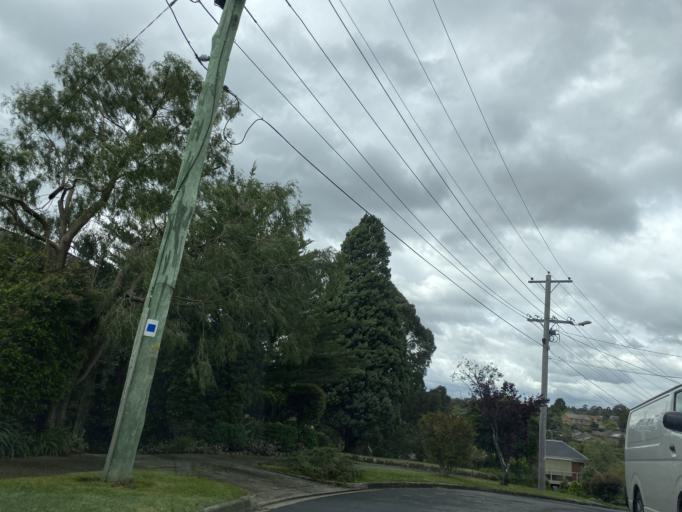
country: AU
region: Victoria
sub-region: Banyule
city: Darch
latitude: -37.7562
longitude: 145.1385
